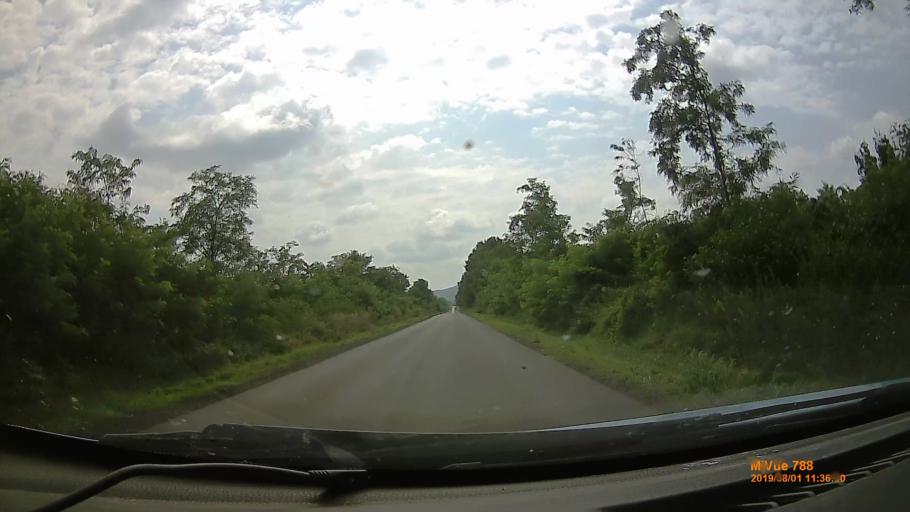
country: HU
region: Baranya
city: Villany
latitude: 45.9130
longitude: 18.3784
